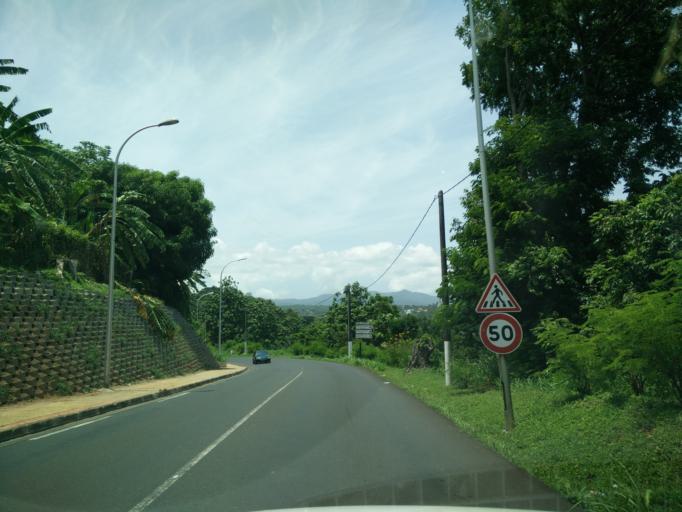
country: GP
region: Guadeloupe
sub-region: Guadeloupe
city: Petit-Bourg
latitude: 16.1980
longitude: -61.5976
